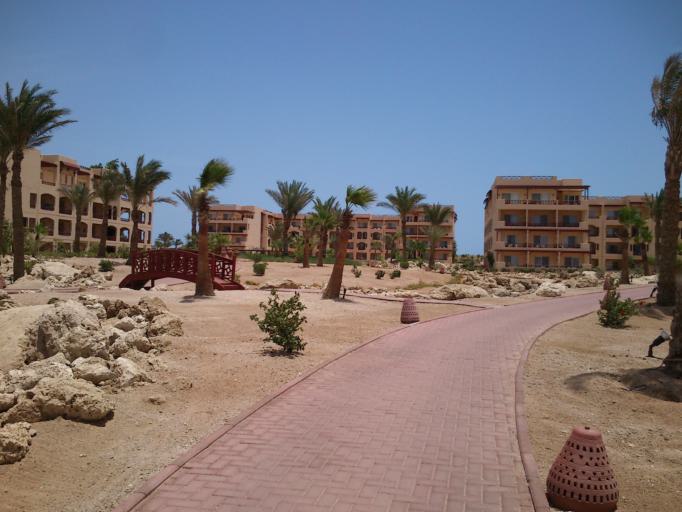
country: EG
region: Red Sea
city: Bur Safajah
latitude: 26.8474
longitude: 33.9908
